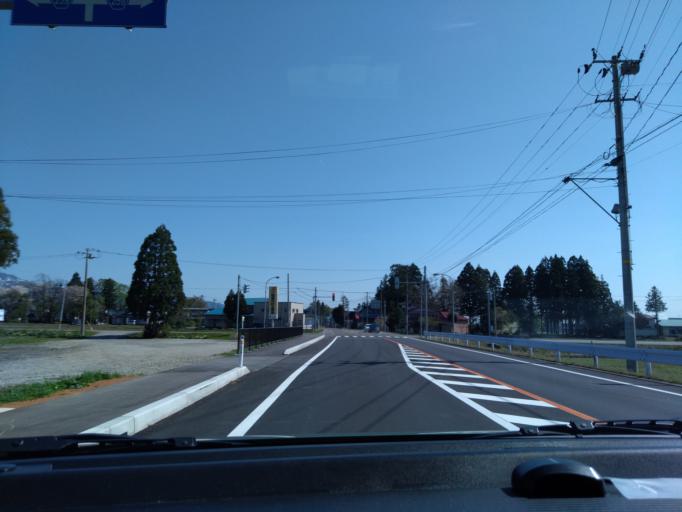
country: JP
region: Akita
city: Kakunodatemachi
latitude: 39.5332
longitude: 140.5853
